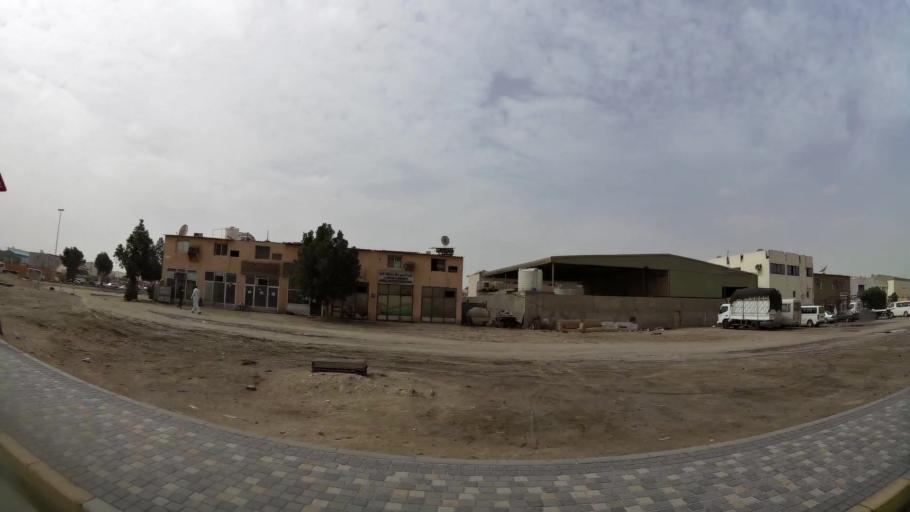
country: AE
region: Abu Dhabi
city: Abu Dhabi
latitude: 24.3560
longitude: 54.5166
